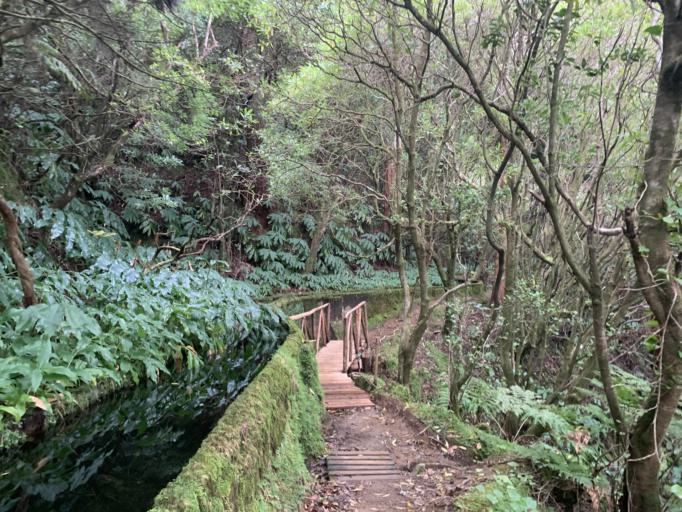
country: PT
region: Azores
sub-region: Vila Franca do Campo
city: Vila Franca do Campo
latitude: 37.7431
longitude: -25.4745
